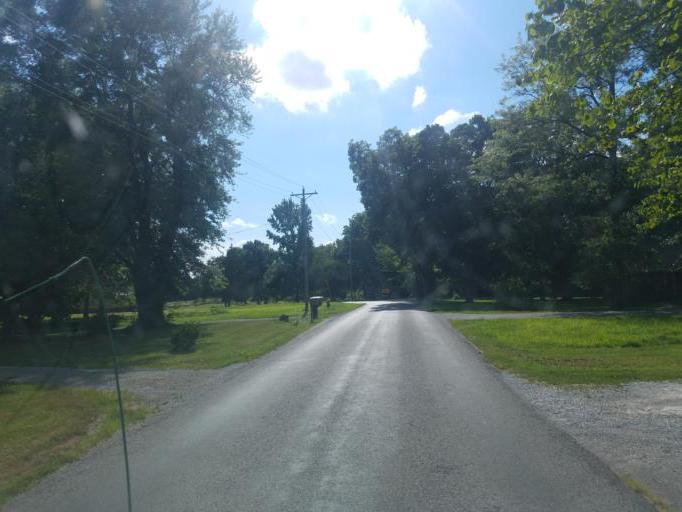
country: US
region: Illinois
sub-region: Jackson County
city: Murphysboro
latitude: 37.7163
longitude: -89.2994
